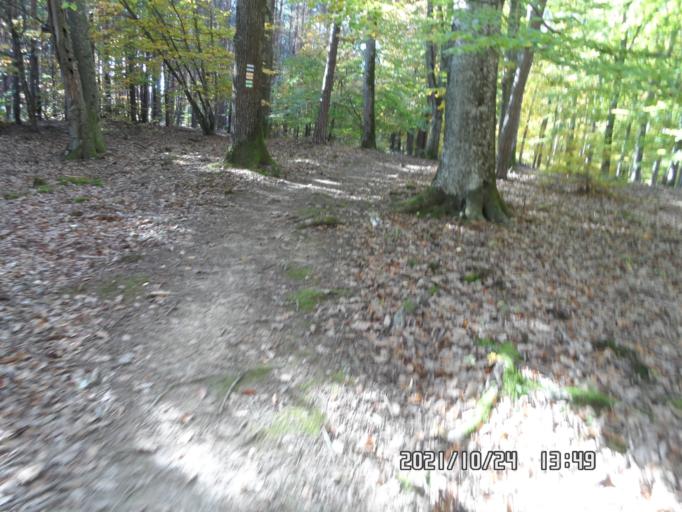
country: SI
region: Hodos-Hodos
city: Hodos
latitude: 46.7789
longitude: 16.3401
